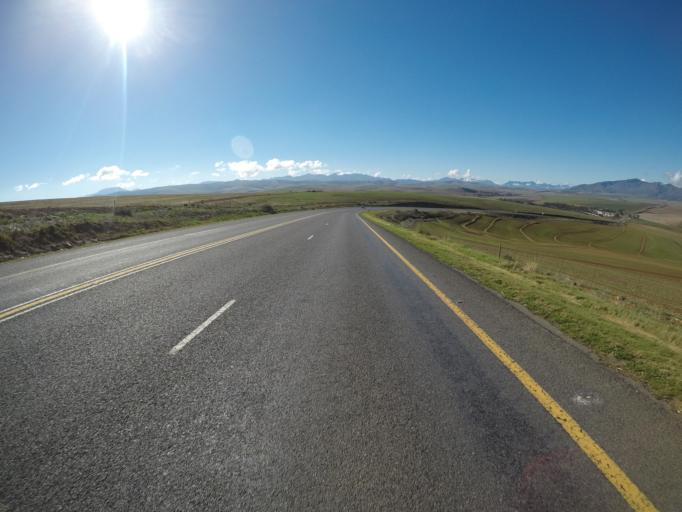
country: ZA
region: Western Cape
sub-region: Overberg District Municipality
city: Caledon
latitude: -34.2138
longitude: 19.3209
